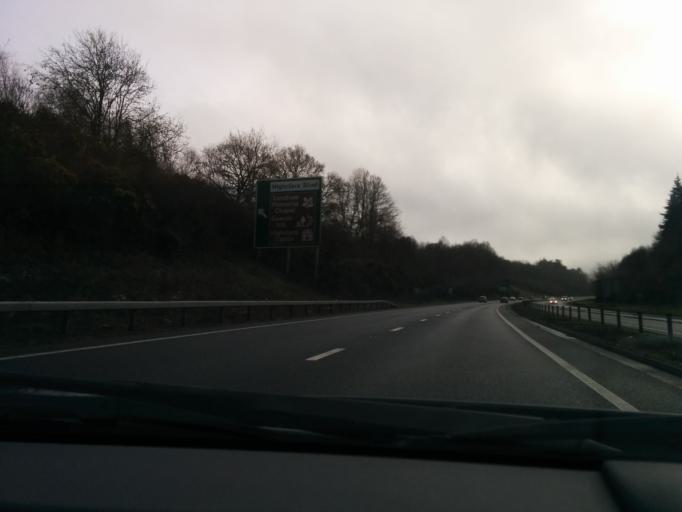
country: GB
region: England
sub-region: Hampshire
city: Highclere
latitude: 51.3560
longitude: -1.3424
